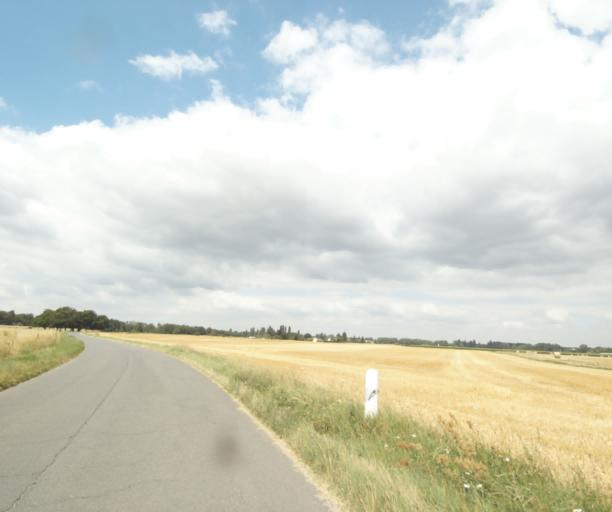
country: FR
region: Centre
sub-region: Departement du Loiret
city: Mardie
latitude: 47.8787
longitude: 2.0439
